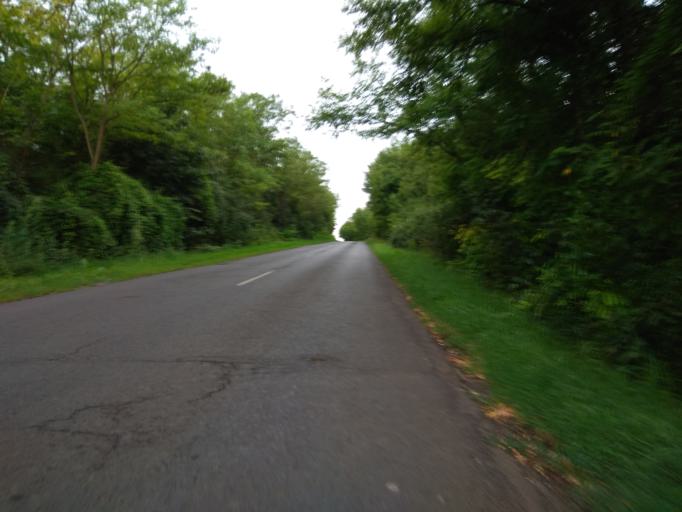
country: HU
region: Borsod-Abauj-Zemplen
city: Monok
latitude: 48.1737
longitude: 21.1151
